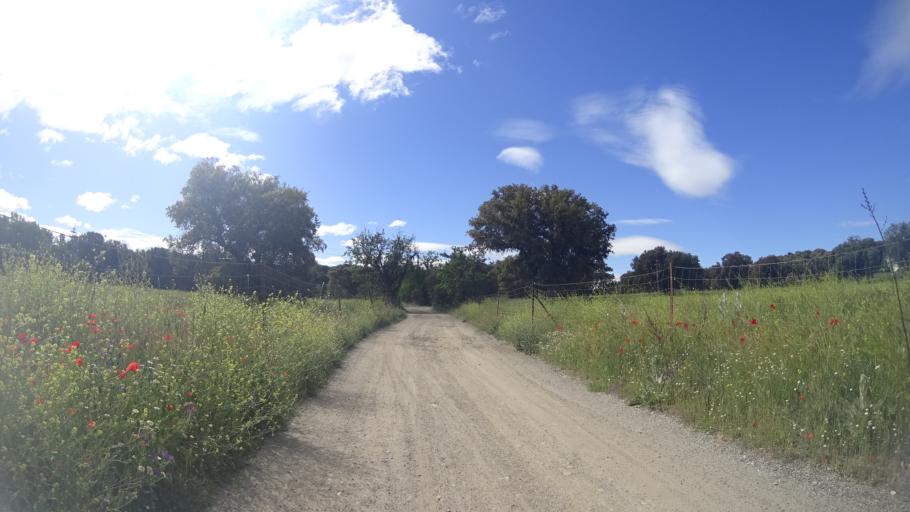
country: ES
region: Madrid
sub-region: Provincia de Madrid
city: Brunete
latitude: 40.4227
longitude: -3.9500
